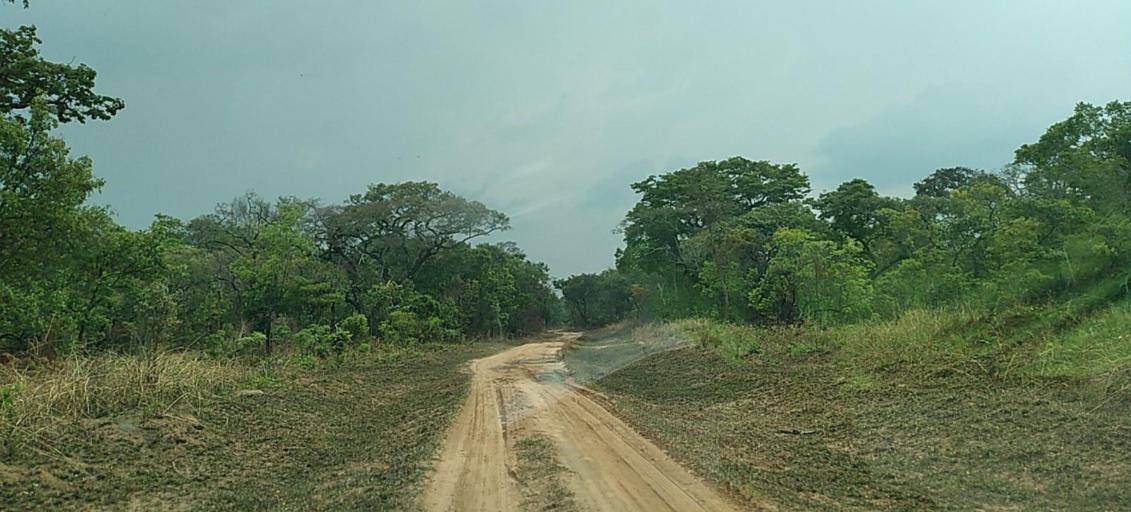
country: ZM
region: North-Western
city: Mwinilunga
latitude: -11.4672
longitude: 24.4691
